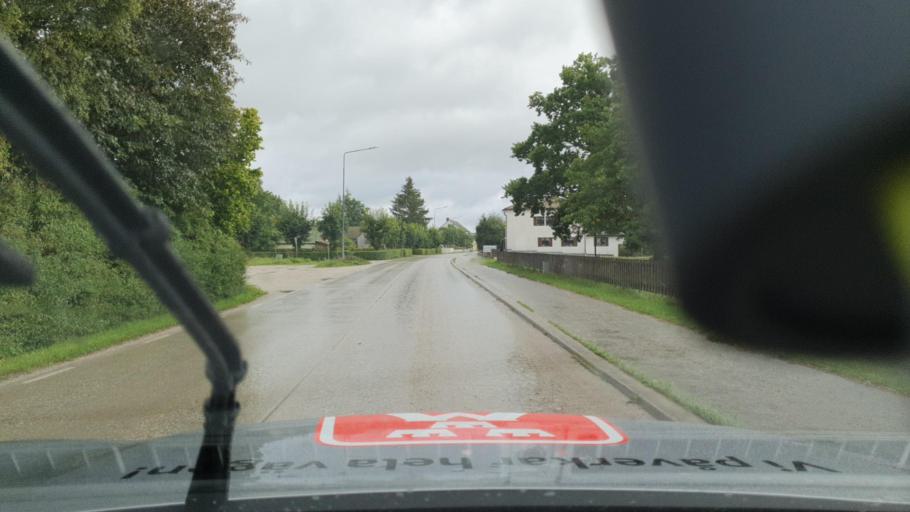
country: SE
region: Gotland
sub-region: Gotland
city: Hemse
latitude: 57.1631
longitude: 18.3339
